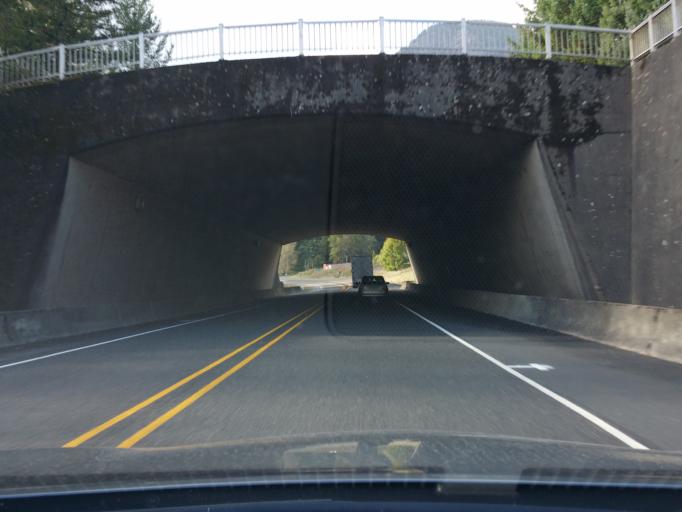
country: US
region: Oregon
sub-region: Hood River County
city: Cascade Locks
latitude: 45.6407
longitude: -121.9821
